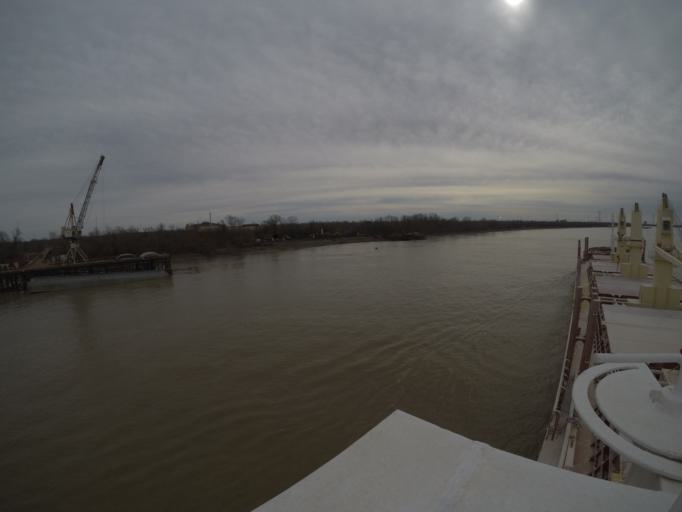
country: US
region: Louisiana
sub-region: Saint John the Baptist Parish
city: Laplace
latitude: 30.0383
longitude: -90.4726
